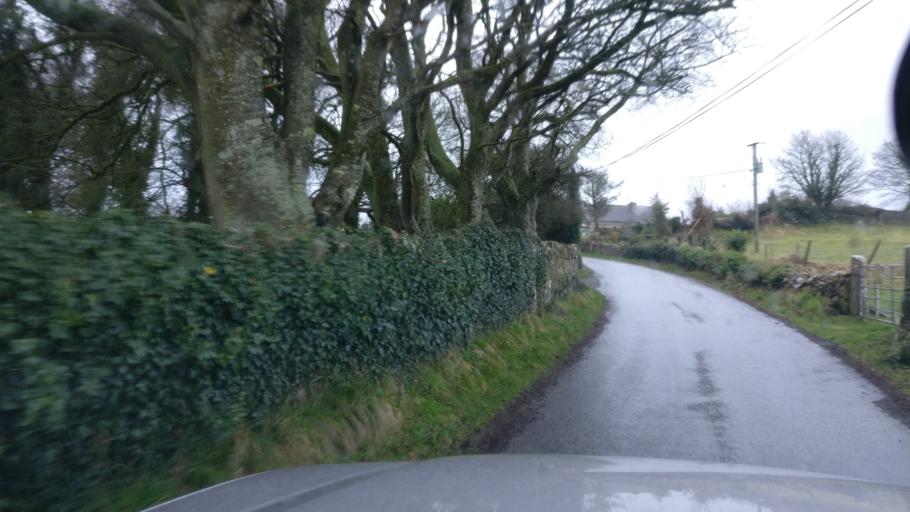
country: IE
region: Connaught
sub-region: County Galway
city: Loughrea
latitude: 53.1795
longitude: -8.6539
